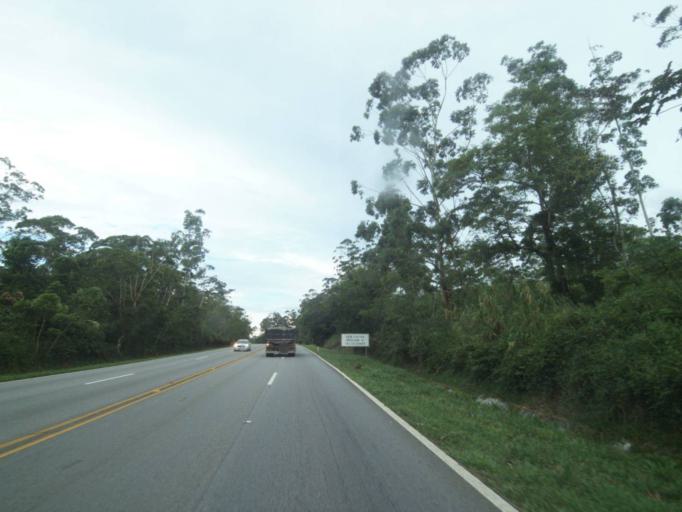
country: BR
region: Parana
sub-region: Paranagua
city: Paranagua
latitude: -25.5996
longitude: -48.6101
